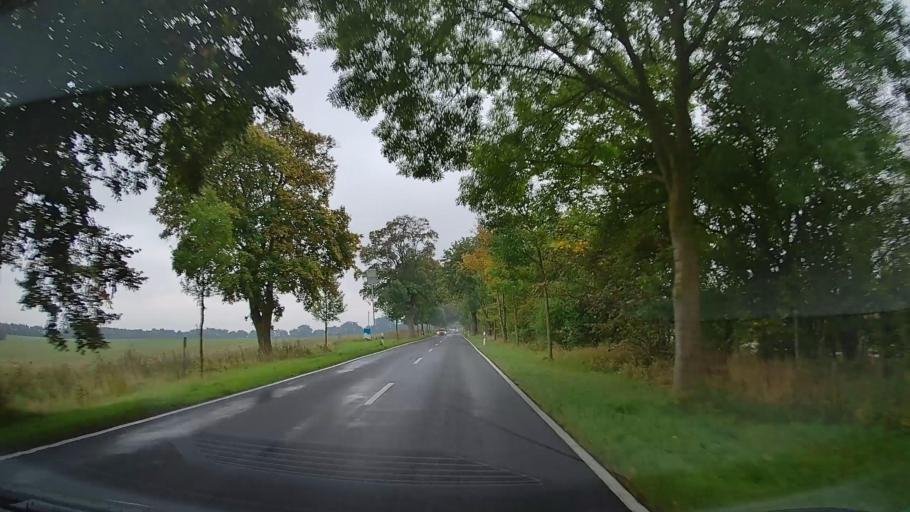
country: DE
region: Mecklenburg-Vorpommern
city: Ostseebad Boltenhagen
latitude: 53.9467
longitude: 11.2347
